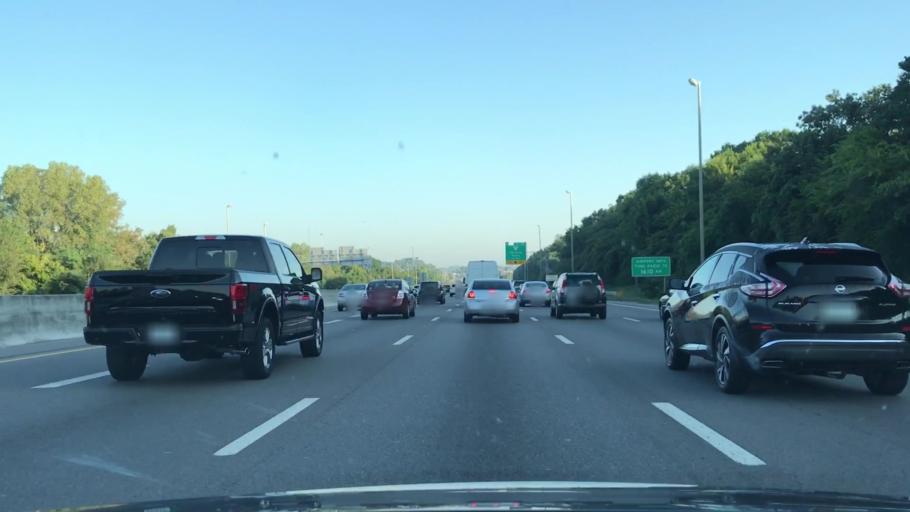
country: US
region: Tennessee
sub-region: Davidson County
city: Oak Hill
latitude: 36.0765
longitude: -86.6940
